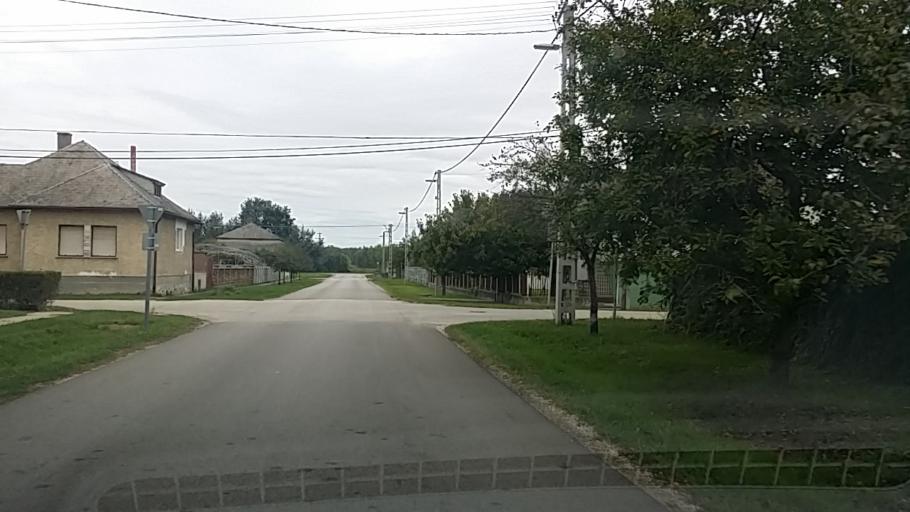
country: HU
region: Komarom-Esztergom
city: Tat
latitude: 47.7416
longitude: 18.6622
